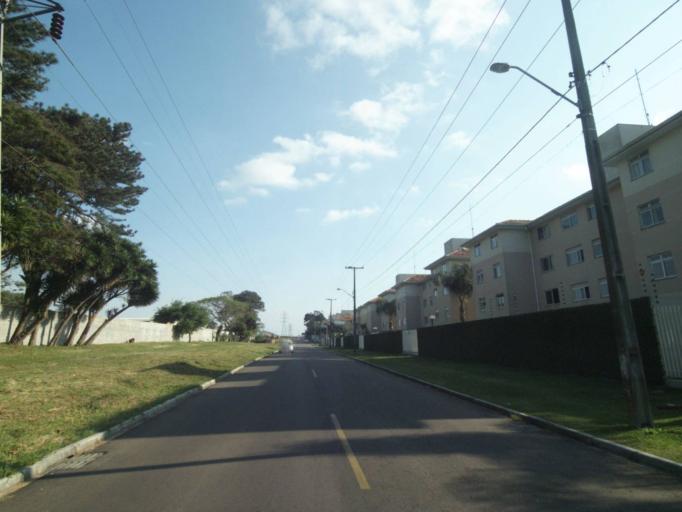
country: BR
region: Parana
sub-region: Curitiba
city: Curitiba
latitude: -25.4853
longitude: -49.3221
